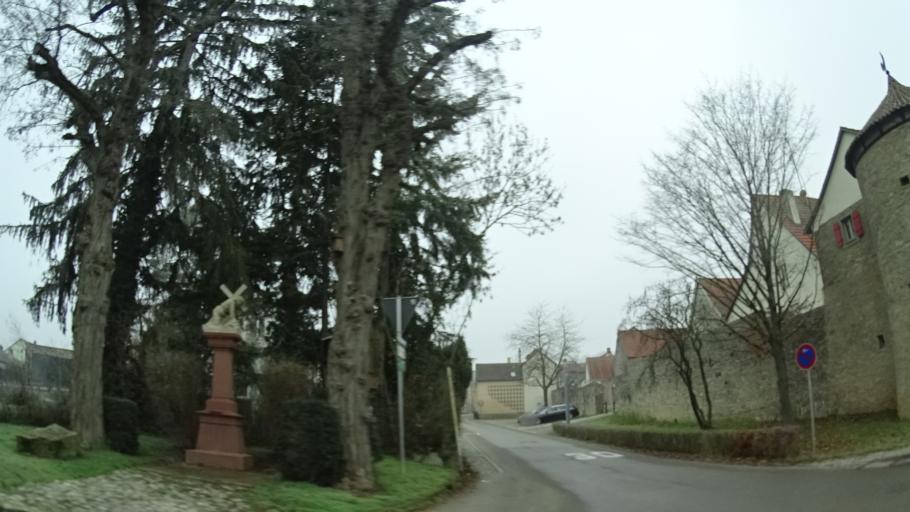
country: DE
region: Bavaria
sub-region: Regierungsbezirk Unterfranken
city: Sulzfeld am Main
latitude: 49.7063
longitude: 10.1327
